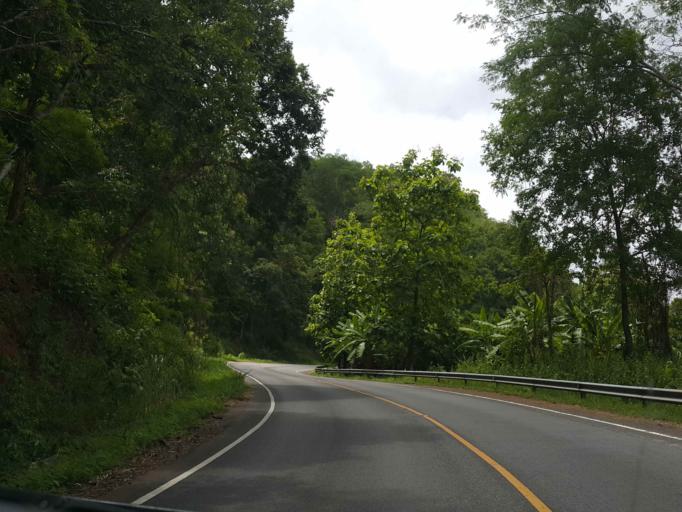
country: TH
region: Chiang Mai
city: Samoeng
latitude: 18.8100
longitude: 98.7894
